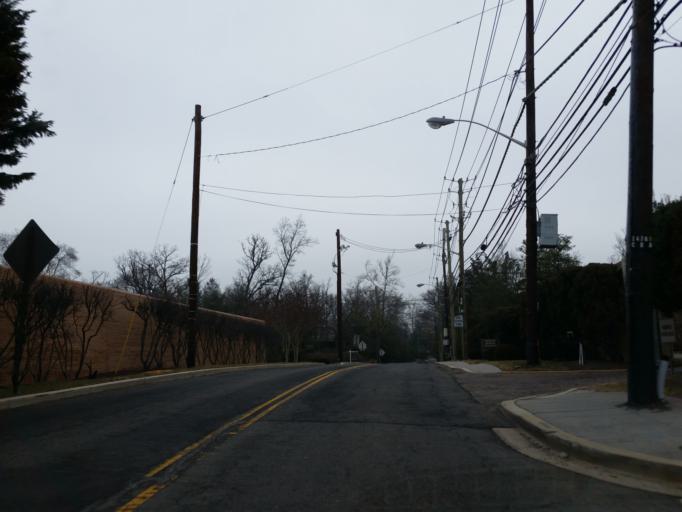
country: US
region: Maryland
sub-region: Montgomery County
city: Brookmont
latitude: 38.9213
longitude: -77.0892
